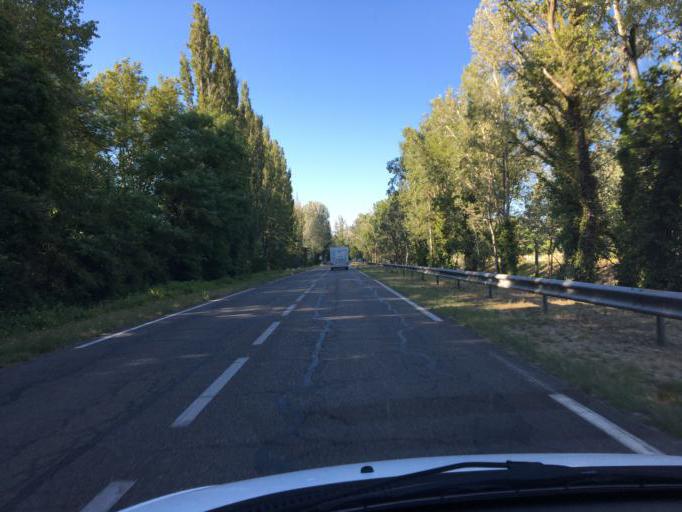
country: FR
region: Provence-Alpes-Cote d'Azur
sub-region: Departement du Vaucluse
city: Avignon
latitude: 43.9676
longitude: 4.8187
